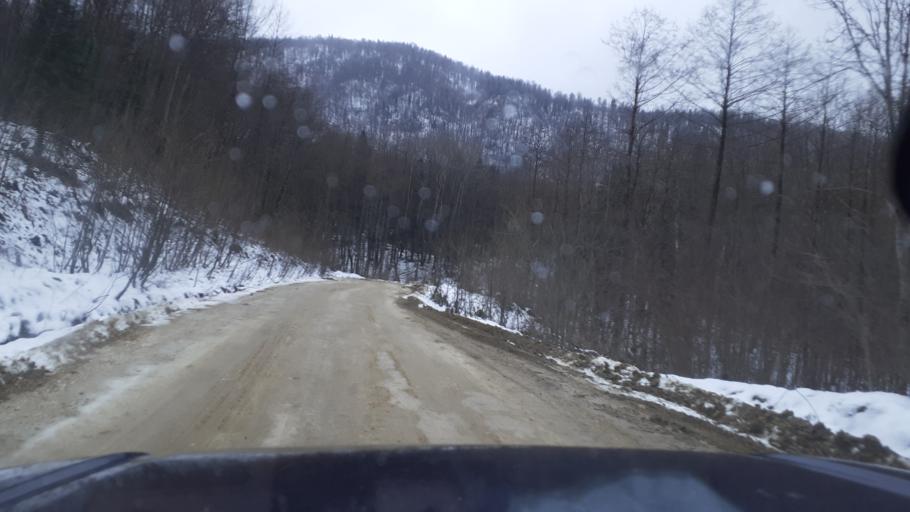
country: RU
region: Krasnodarskiy
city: Neftegorsk
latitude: 44.1487
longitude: 39.8056
